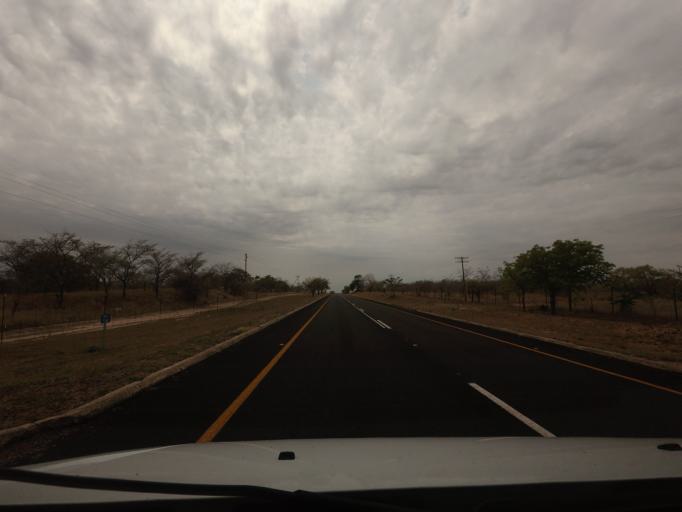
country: ZA
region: Limpopo
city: Thulamahashi
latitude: -24.5606
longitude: 31.1663
